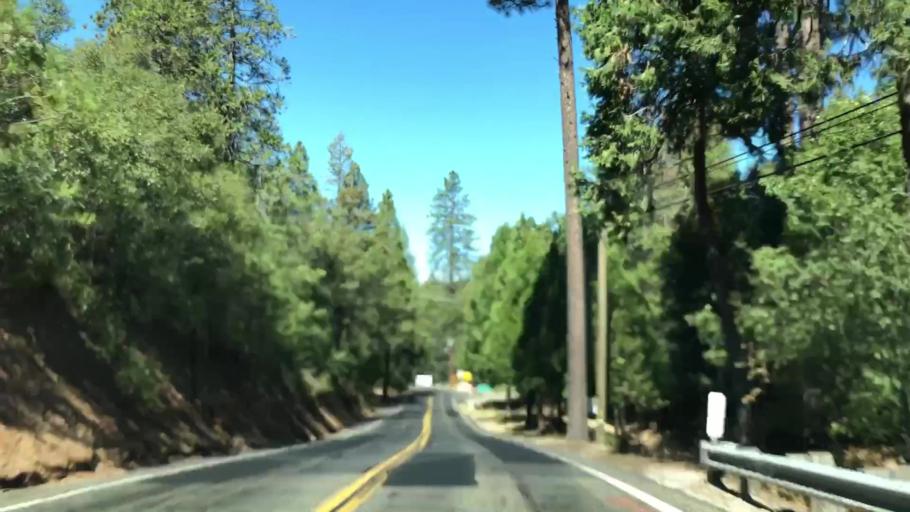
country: US
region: California
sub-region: Tuolumne County
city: Tuolumne City
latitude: 37.8388
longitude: -120.2223
